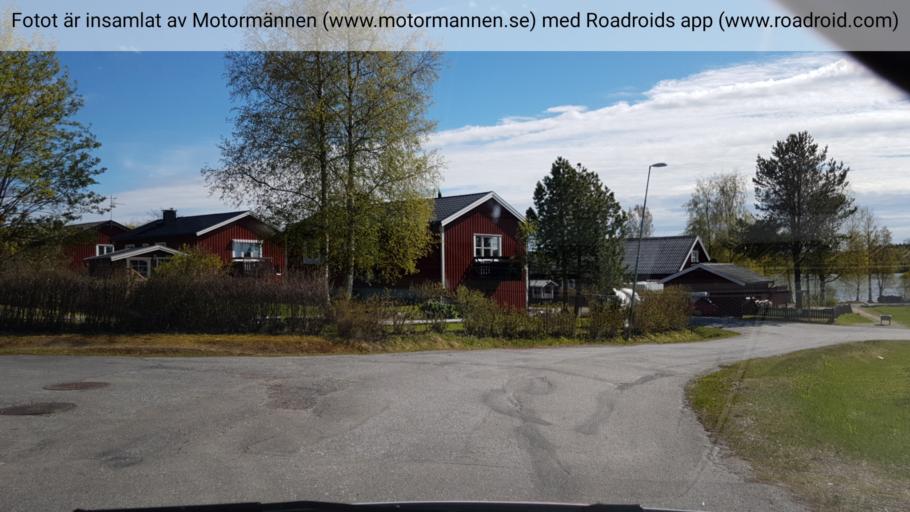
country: SE
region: Vaesterbotten
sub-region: Umea Kommun
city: Roback
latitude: 64.0394
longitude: 20.0693
